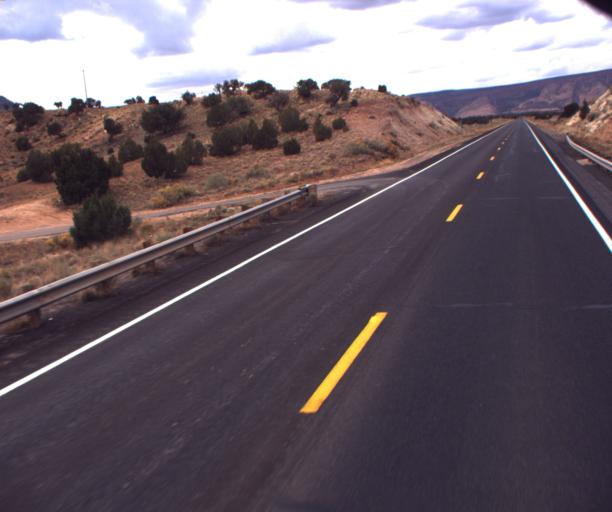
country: US
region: Arizona
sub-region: Navajo County
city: Kayenta
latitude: 36.6988
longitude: -110.3265
